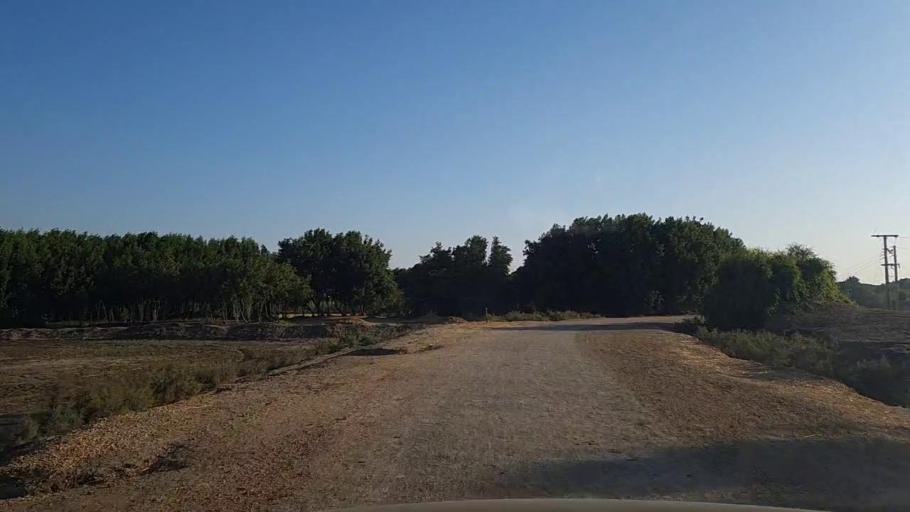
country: PK
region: Sindh
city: Mirpur Batoro
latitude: 24.7099
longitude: 68.3205
